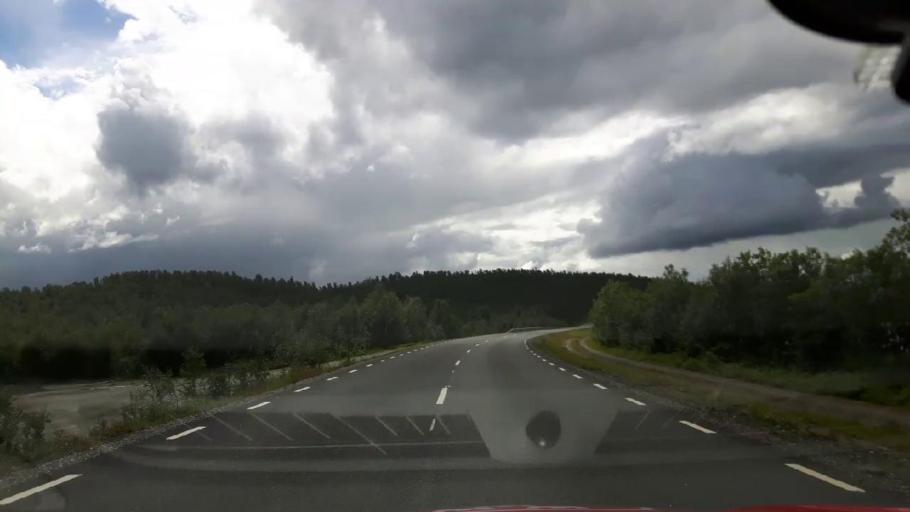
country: NO
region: Nord-Trondelag
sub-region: Royrvik
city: Royrvik
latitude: 64.9787
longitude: 14.2141
